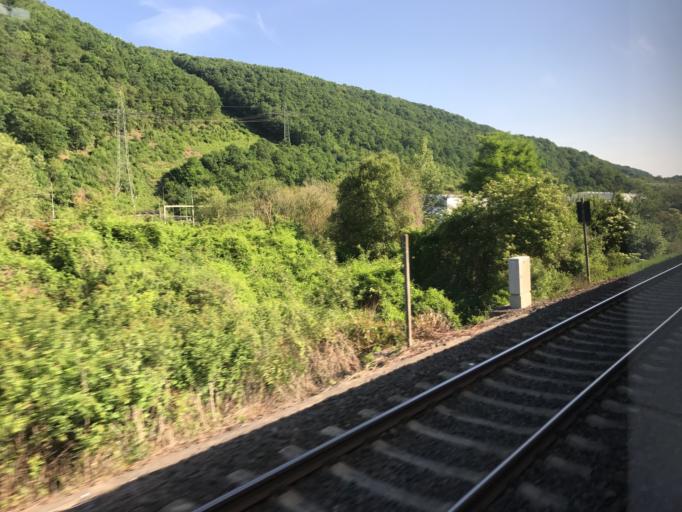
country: DE
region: Rheinland-Pfalz
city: Barenbach
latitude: 49.7670
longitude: 7.4400
